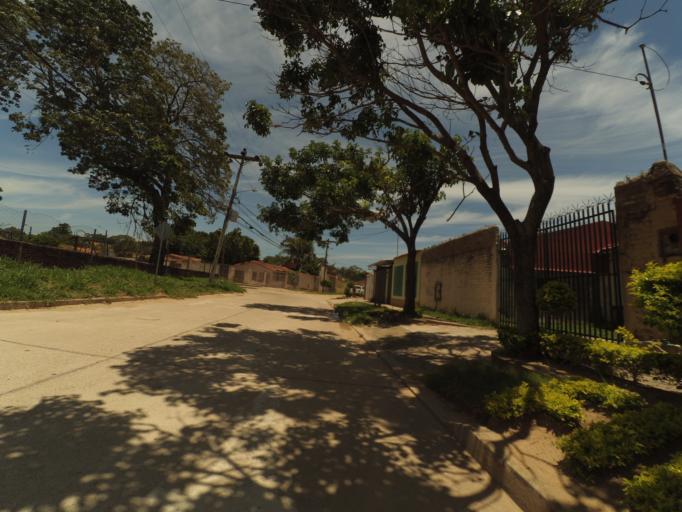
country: BO
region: Santa Cruz
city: Santa Cruz de la Sierra
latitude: -17.8113
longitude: -63.2259
